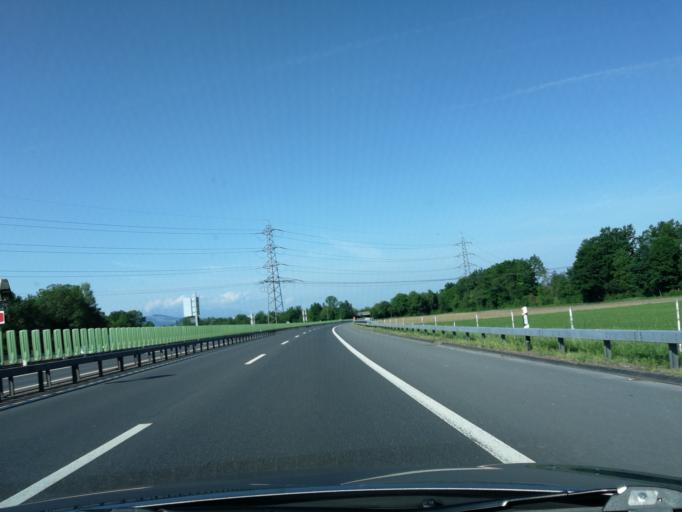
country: CH
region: Zug
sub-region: Zug
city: Steinhausen
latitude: 47.1924
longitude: 8.5056
